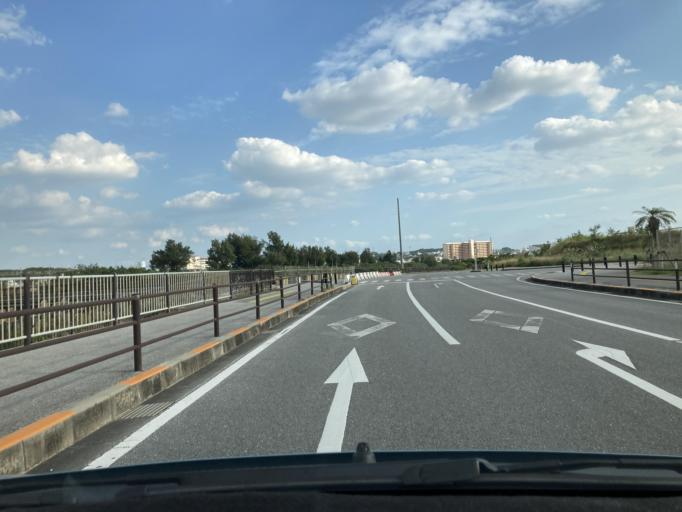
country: JP
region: Okinawa
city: Itoman
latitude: 26.1582
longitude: 127.6645
